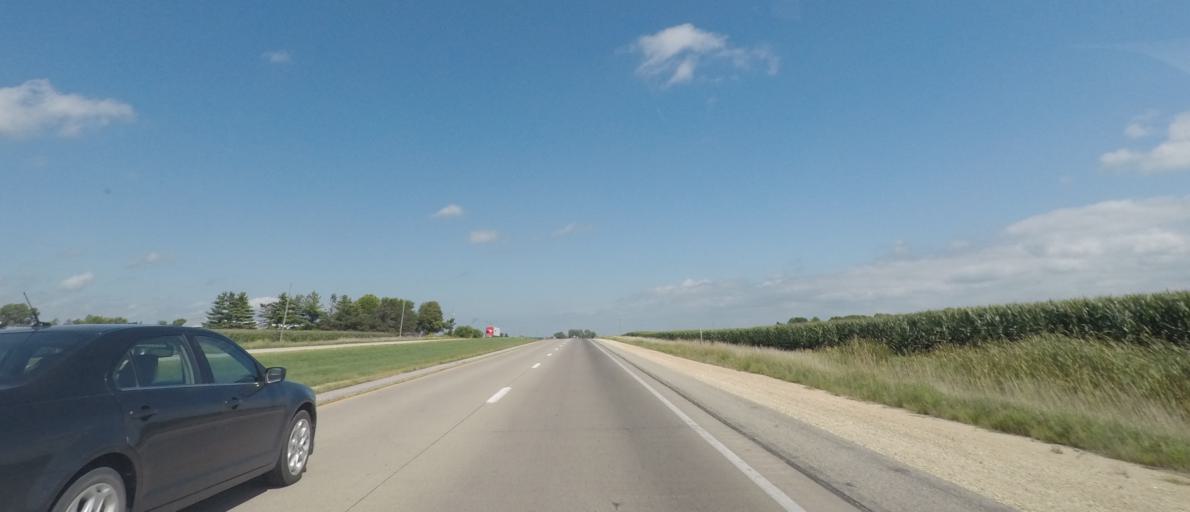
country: US
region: Iowa
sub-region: Linn County
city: Marion
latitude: 42.0388
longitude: -91.5255
